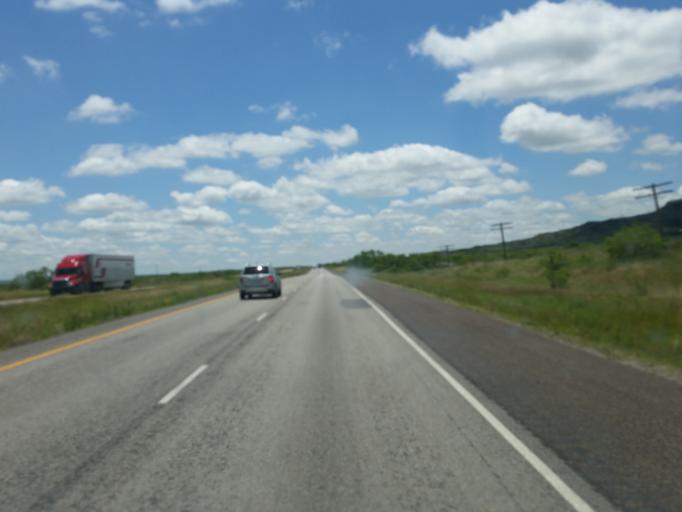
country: US
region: Texas
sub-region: Scurry County
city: Snyder
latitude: 32.9694
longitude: -101.0979
